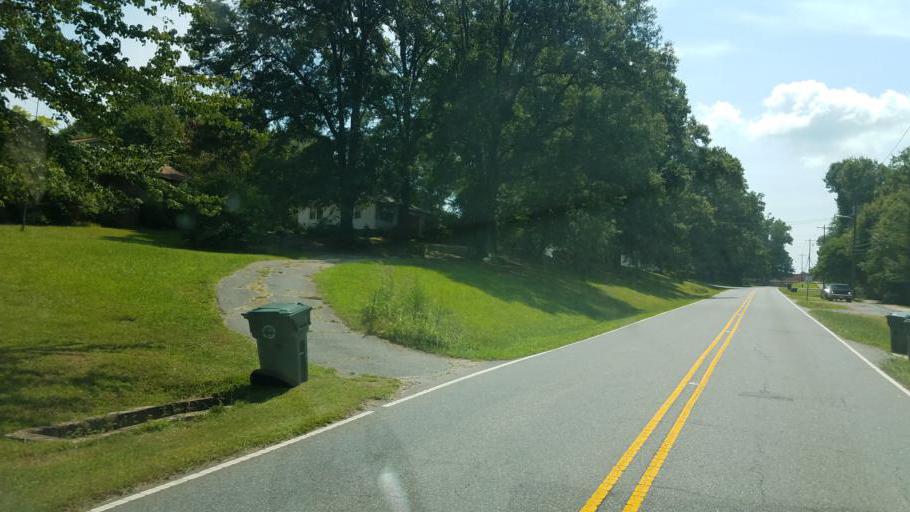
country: US
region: North Carolina
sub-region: Gaston County
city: Cherryville
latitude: 35.3878
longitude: -81.3865
